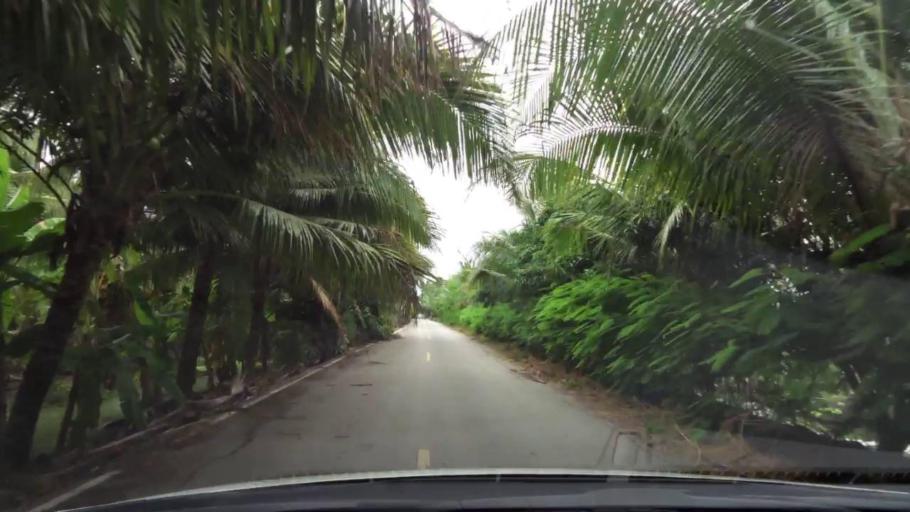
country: TH
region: Ratchaburi
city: Damnoen Saduak
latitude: 13.5511
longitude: 99.9731
